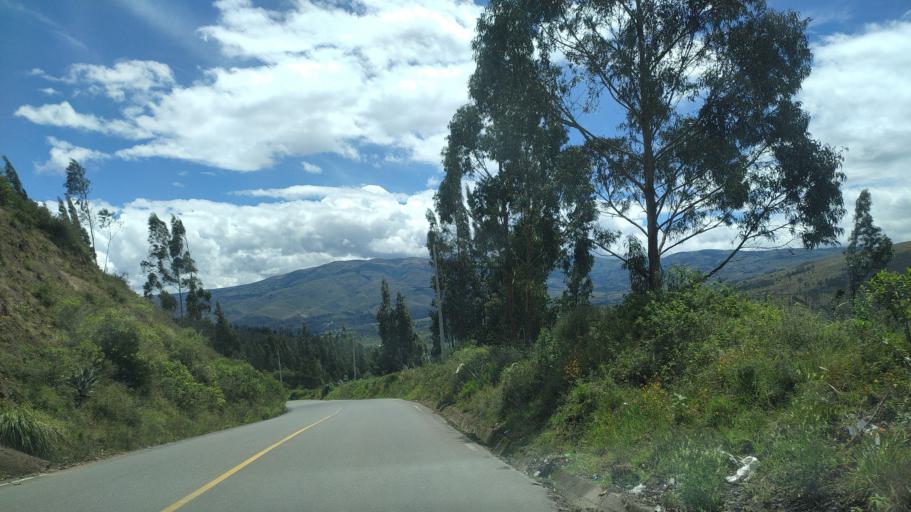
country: EC
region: Chimborazo
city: Riobamba
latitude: -1.6614
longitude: -78.5812
